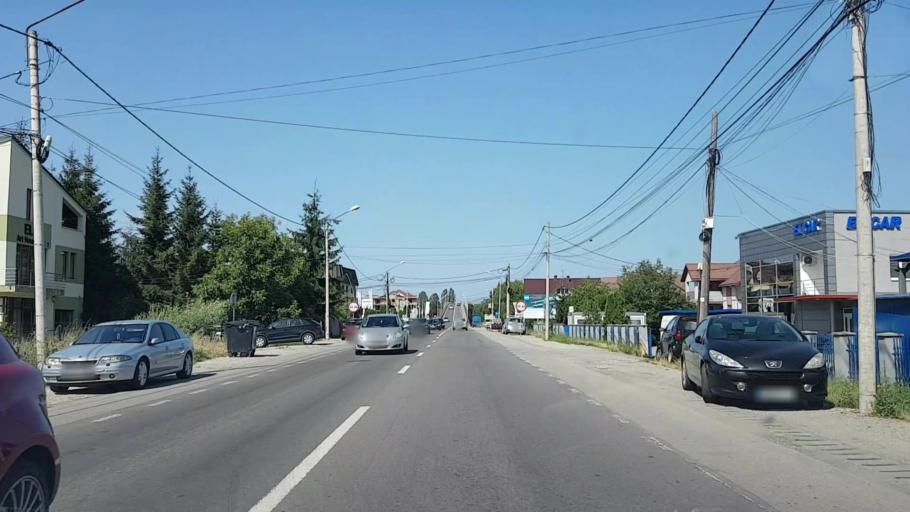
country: RO
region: Bistrita-Nasaud
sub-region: Municipiul Bistrita
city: Viisoara
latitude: 47.1133
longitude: 24.4619
